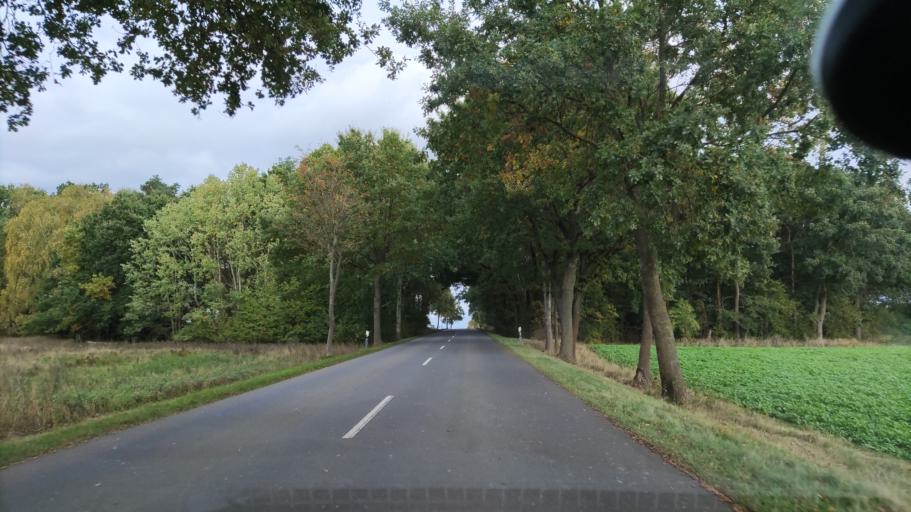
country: DE
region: Lower Saxony
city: Romstedt
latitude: 53.0855
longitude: 10.6409
